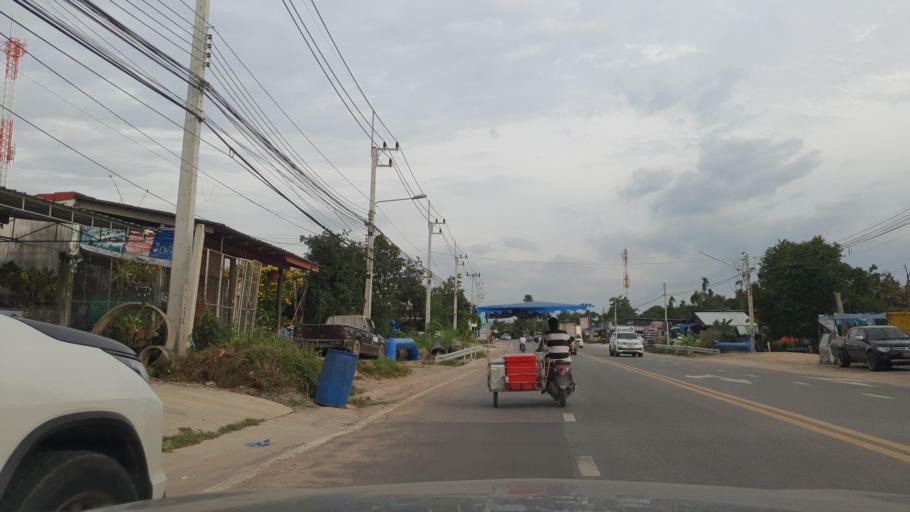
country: TH
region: Chon Buri
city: Phatthaya
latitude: 12.9439
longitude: 100.9404
